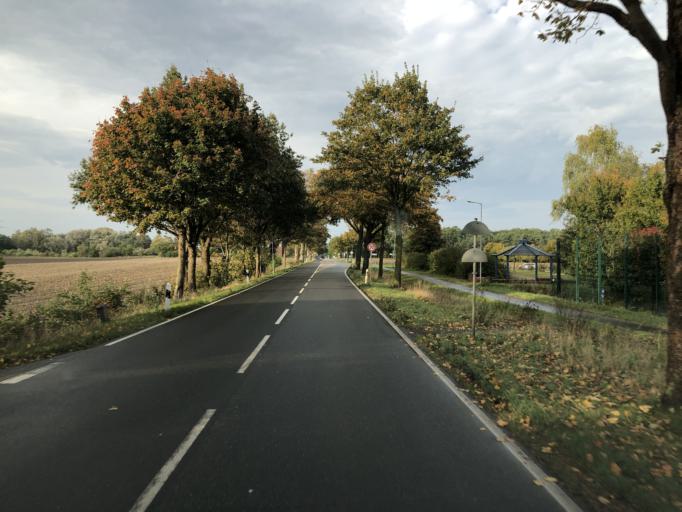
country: DE
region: Lower Saxony
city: Neu Wulmstorf
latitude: 53.4485
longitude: 9.7994
